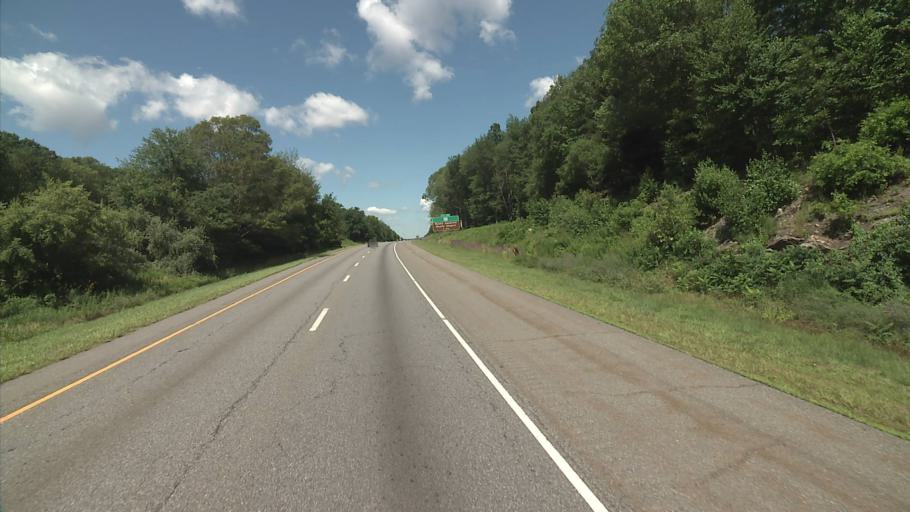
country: US
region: Connecticut
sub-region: New London County
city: Old Mystic
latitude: 41.3724
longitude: -71.9339
